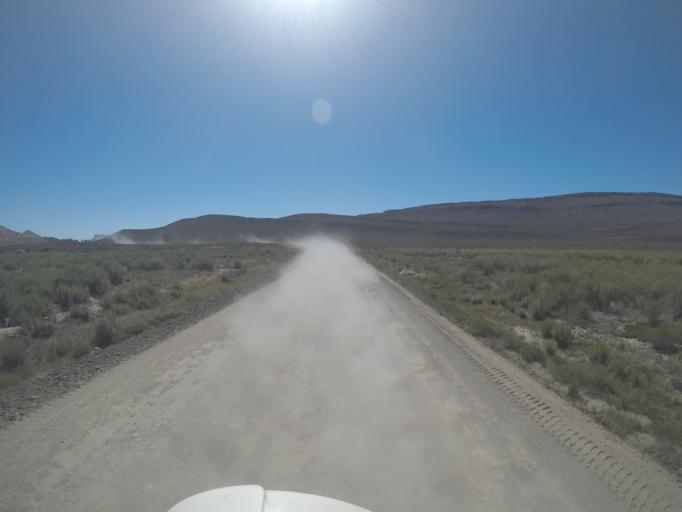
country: ZA
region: Western Cape
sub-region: Cape Winelands District Municipality
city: Ceres
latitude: -32.8290
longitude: 19.4540
